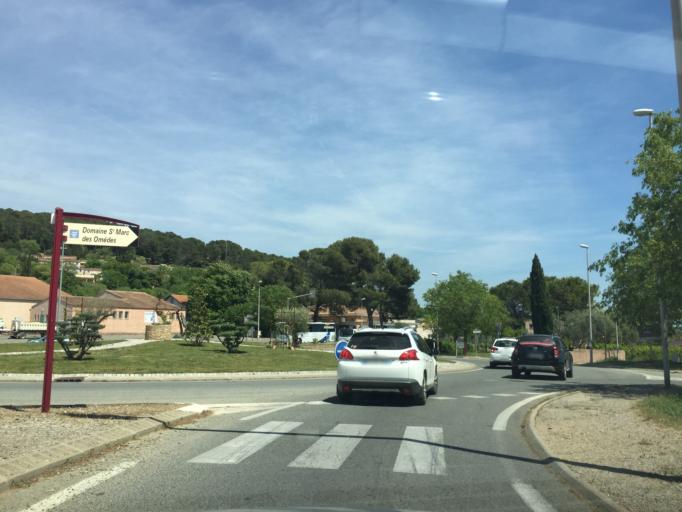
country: FR
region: Provence-Alpes-Cote d'Azur
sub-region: Departement du Var
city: Lorgues
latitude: 43.4919
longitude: 6.3679
